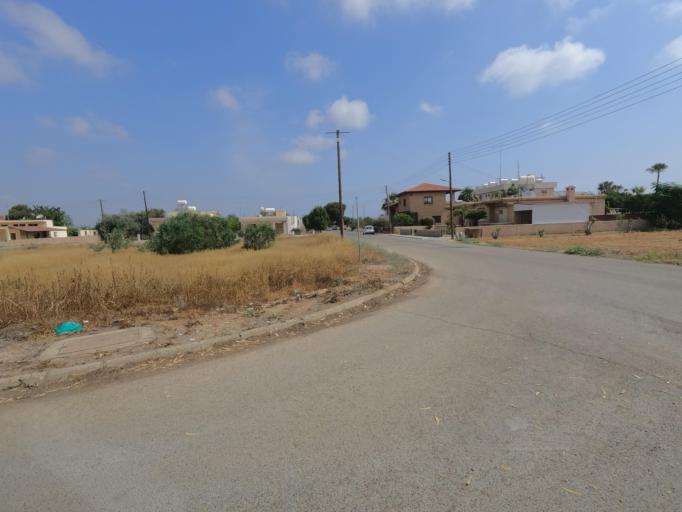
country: CY
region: Ammochostos
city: Deryneia
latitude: 35.0547
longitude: 33.9566
